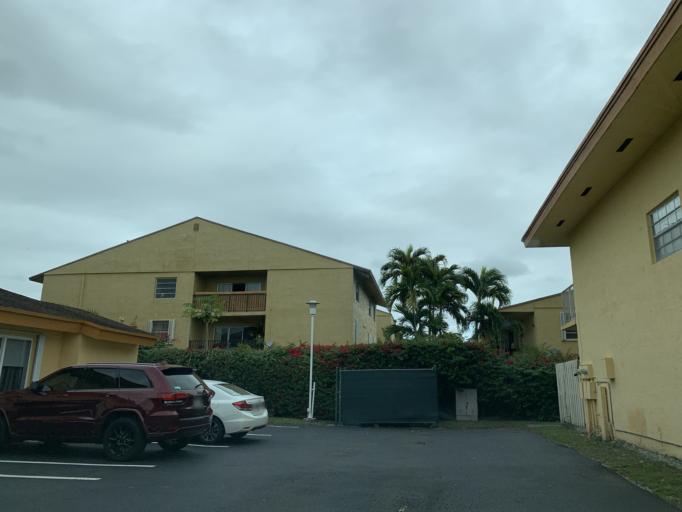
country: US
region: Florida
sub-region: Miami-Dade County
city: The Hammocks
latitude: 25.6892
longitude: -80.4435
